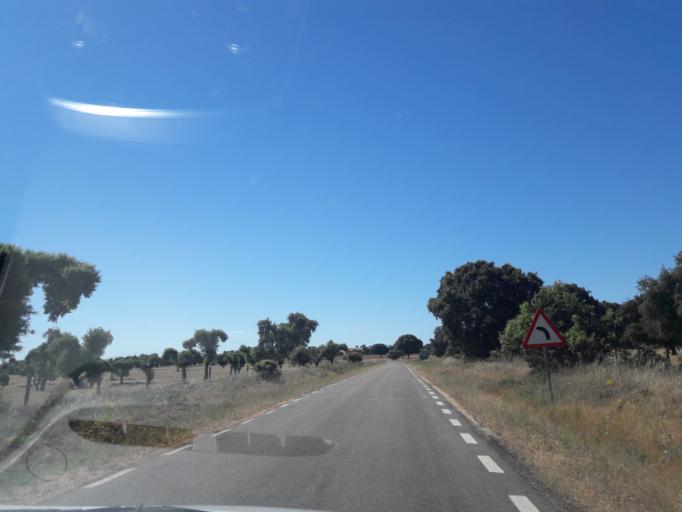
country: ES
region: Castille and Leon
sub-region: Provincia de Salamanca
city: Zarapicos
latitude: 41.0261
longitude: -5.8348
